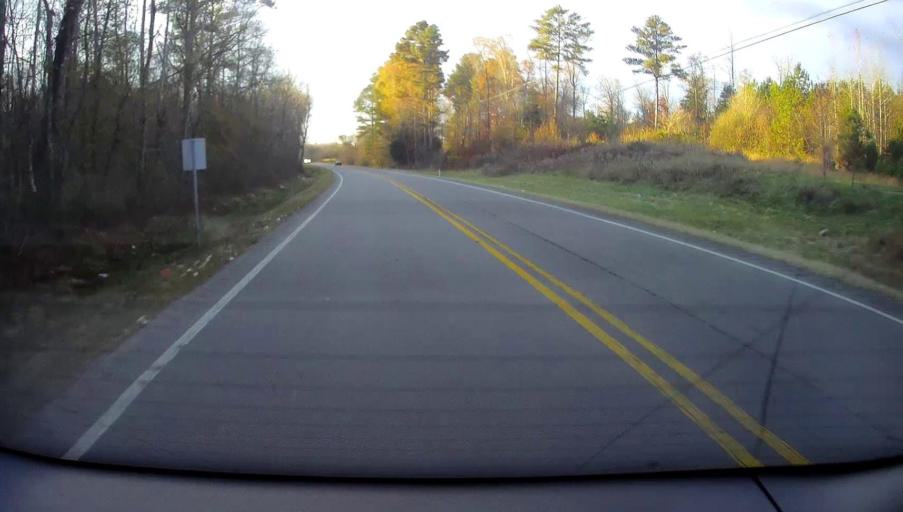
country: US
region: Alabama
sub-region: Blount County
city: Blountsville
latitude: 34.1536
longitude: -86.4565
